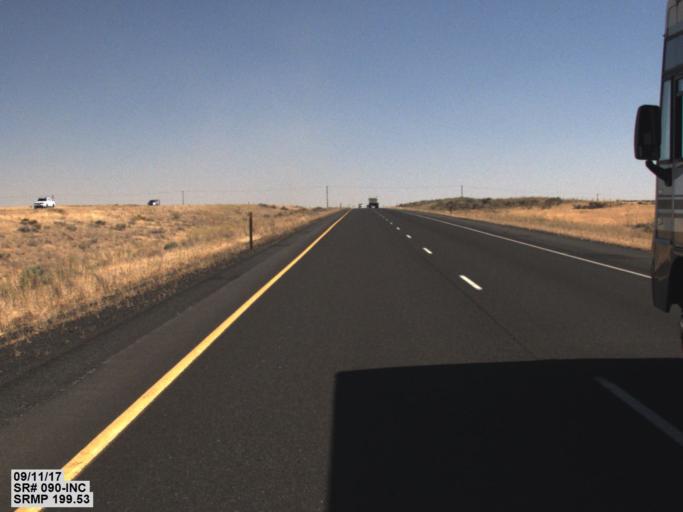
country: US
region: Washington
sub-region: Grant County
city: Warden
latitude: 47.0859
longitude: -118.8197
